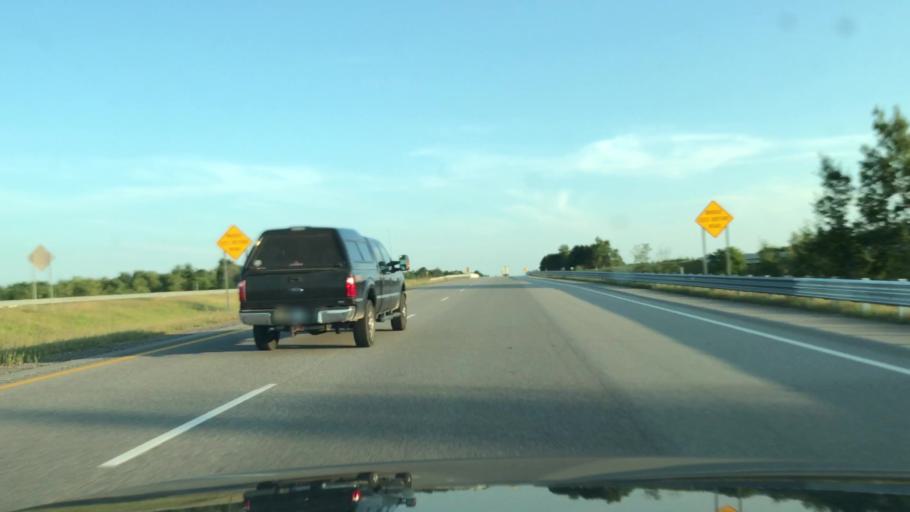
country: US
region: Michigan
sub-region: Osceola County
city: Reed City
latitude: 43.8862
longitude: -85.5282
